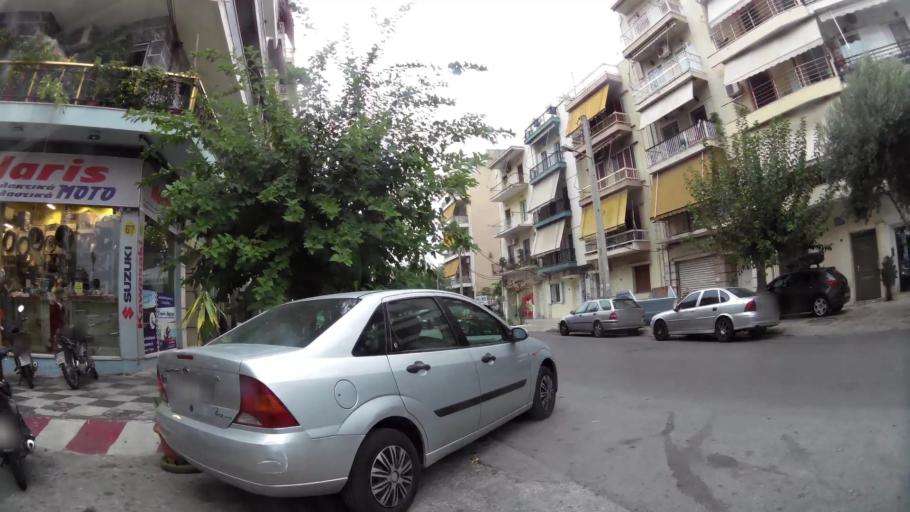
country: GR
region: Attica
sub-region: Nomos Piraios
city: Nikaia
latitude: 37.9544
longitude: 23.6549
